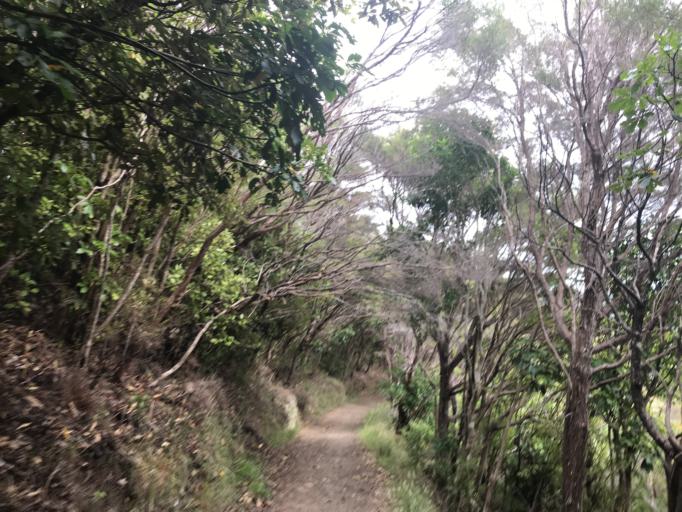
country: NZ
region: Marlborough
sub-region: Marlborough District
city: Picton
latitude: -41.2162
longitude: 173.9786
